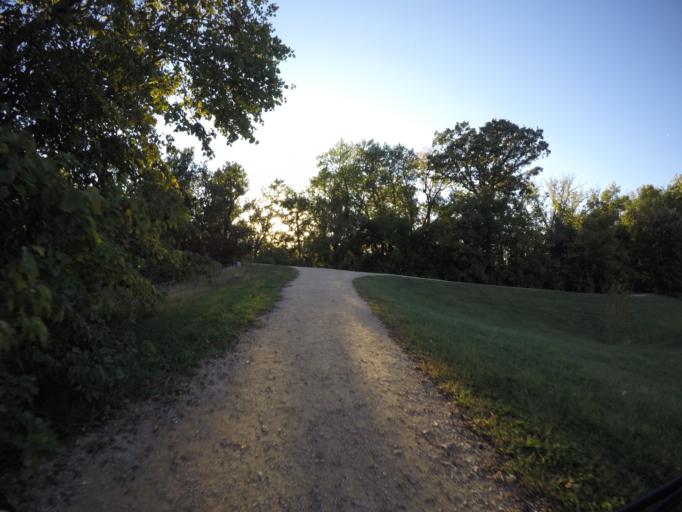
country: US
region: Kansas
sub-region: Riley County
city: Manhattan
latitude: 39.1860
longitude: -96.6348
